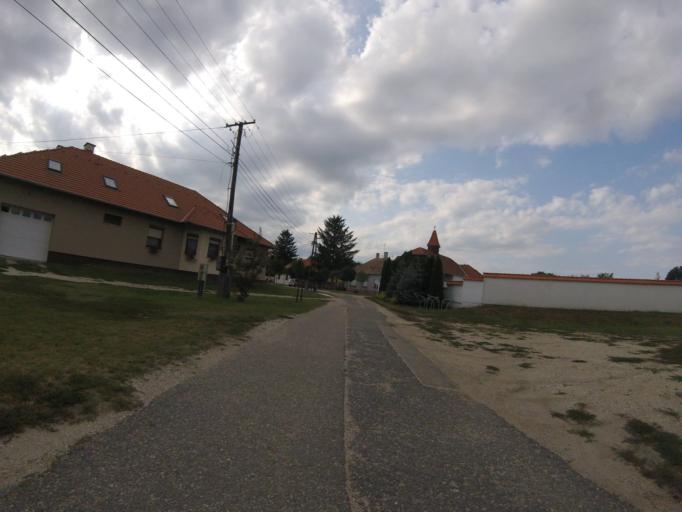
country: HU
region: Gyor-Moson-Sopron
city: Fertod
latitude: 47.6354
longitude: 16.8658
